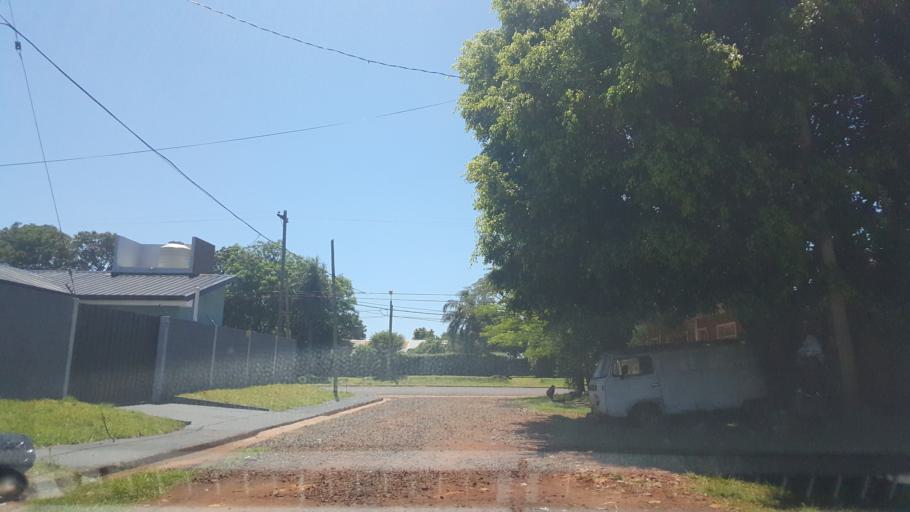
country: AR
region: Misiones
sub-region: Departamento de Capital
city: Posadas
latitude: -27.3866
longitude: -55.9312
